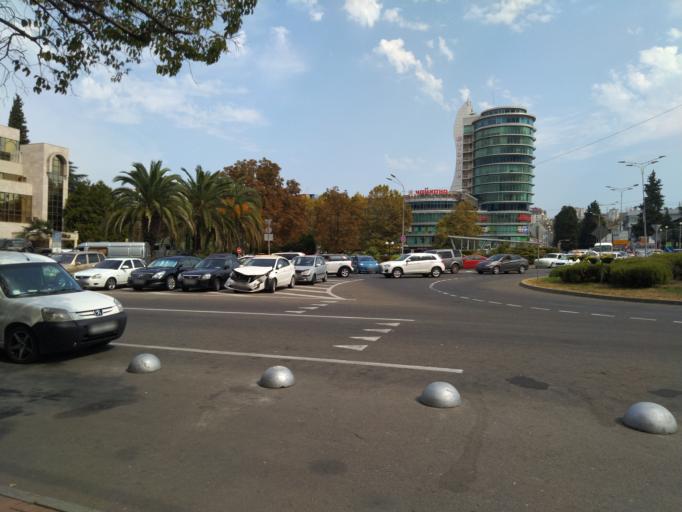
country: RU
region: Krasnodarskiy
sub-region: Sochi City
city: Sochi
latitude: 43.5949
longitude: 39.7207
